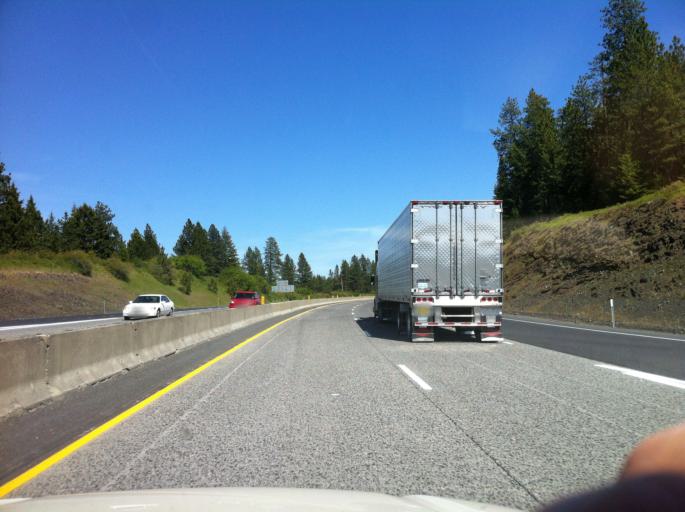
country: US
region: Oregon
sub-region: Umatilla County
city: Mission
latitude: 45.5996
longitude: -118.5073
